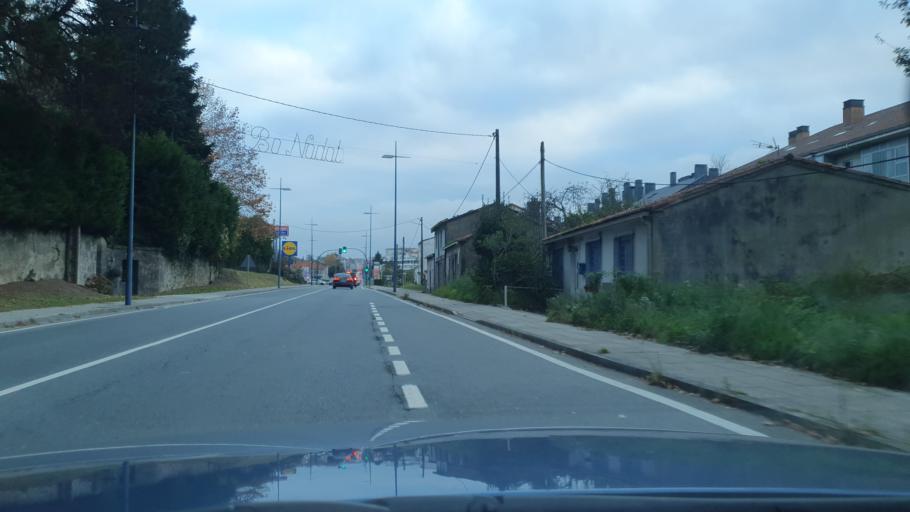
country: ES
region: Galicia
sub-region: Provincia da Coruna
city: Santiago de Compostela
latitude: 42.8650
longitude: -8.5659
